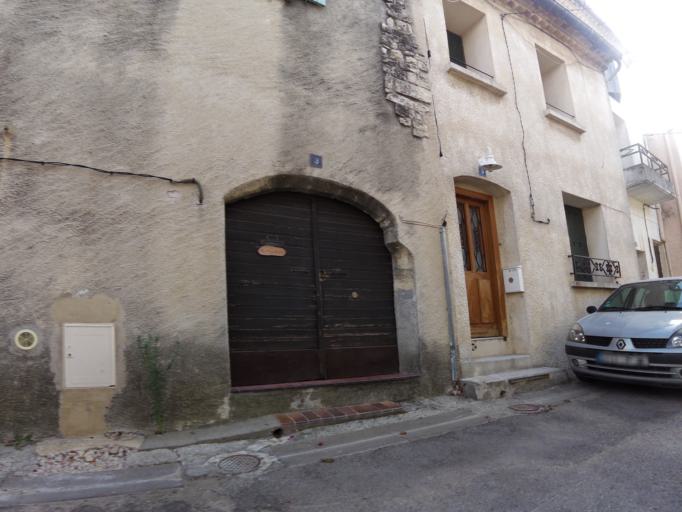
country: FR
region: Languedoc-Roussillon
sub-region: Departement du Gard
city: Calvisson
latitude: 43.7856
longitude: 4.1887
